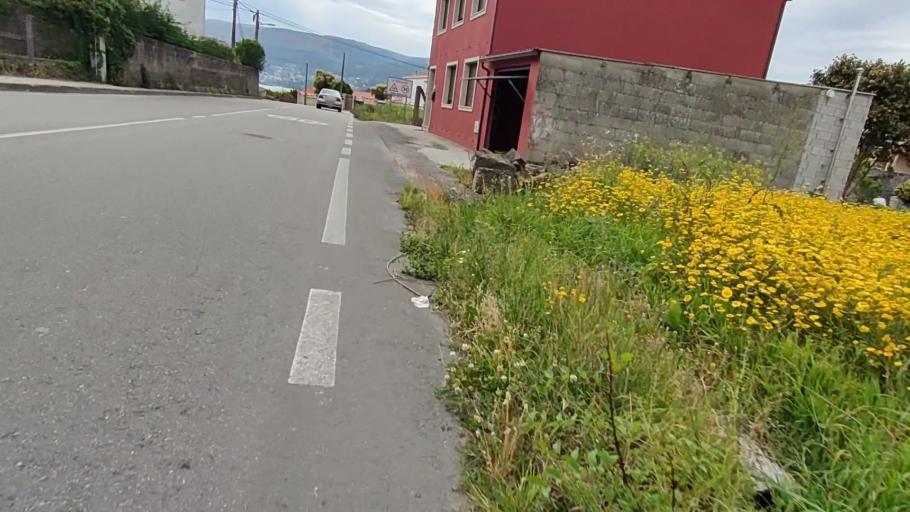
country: ES
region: Galicia
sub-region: Provincia da Coruna
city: Boiro
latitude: 42.6349
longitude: -8.8708
